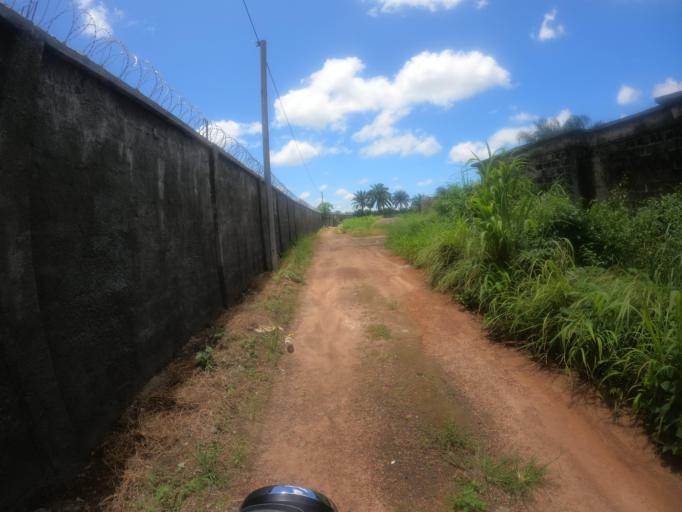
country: SL
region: Northern Province
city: Makeni
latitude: 8.8738
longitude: -12.0950
